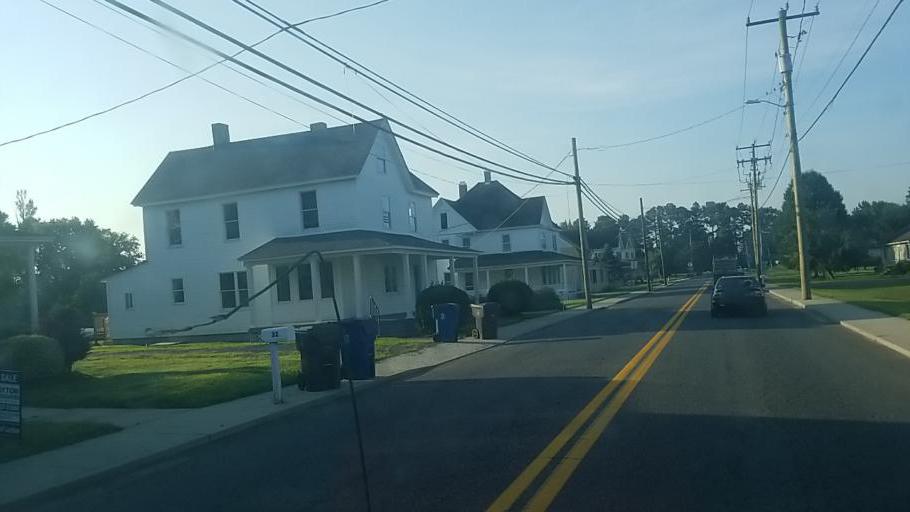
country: US
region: Delaware
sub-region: Sussex County
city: Selbyville
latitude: 38.4576
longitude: -75.2199
